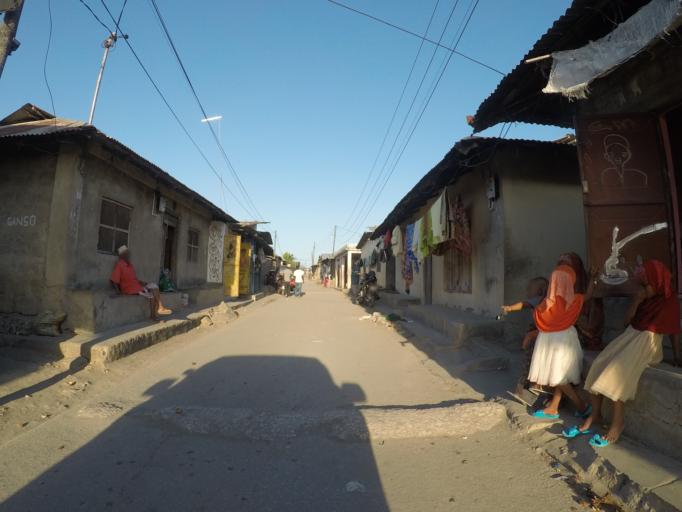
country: TZ
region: Zanzibar Urban/West
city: Zanzibar
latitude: -6.1578
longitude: 39.2123
